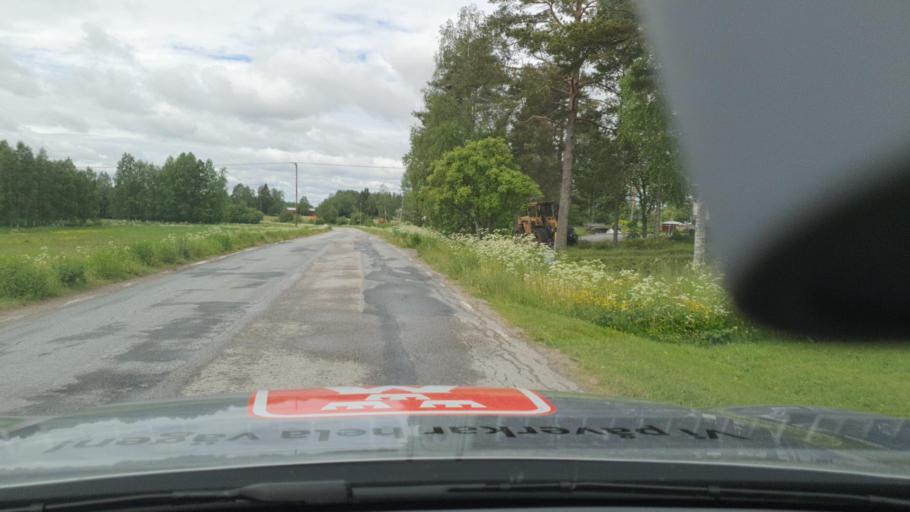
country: SE
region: Norrbotten
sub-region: Lulea Kommun
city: Ranea
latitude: 65.7742
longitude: 22.2433
